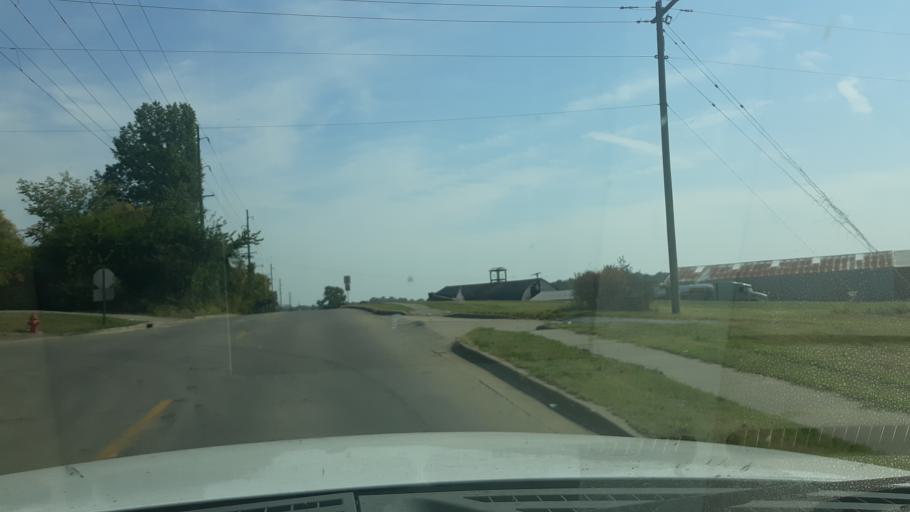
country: US
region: Illinois
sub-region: Saline County
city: Harrisburg
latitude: 37.7203
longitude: -88.5460
